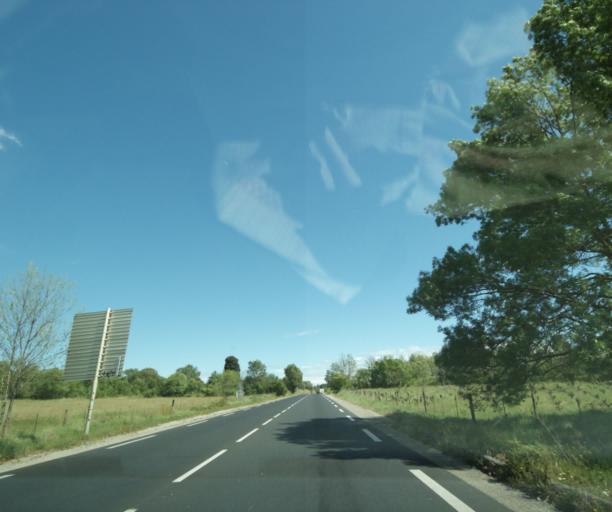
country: FR
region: Languedoc-Roussillon
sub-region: Departement de l'Herault
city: Saint-Jean-de-Vedas
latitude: 43.5886
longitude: 3.8238
